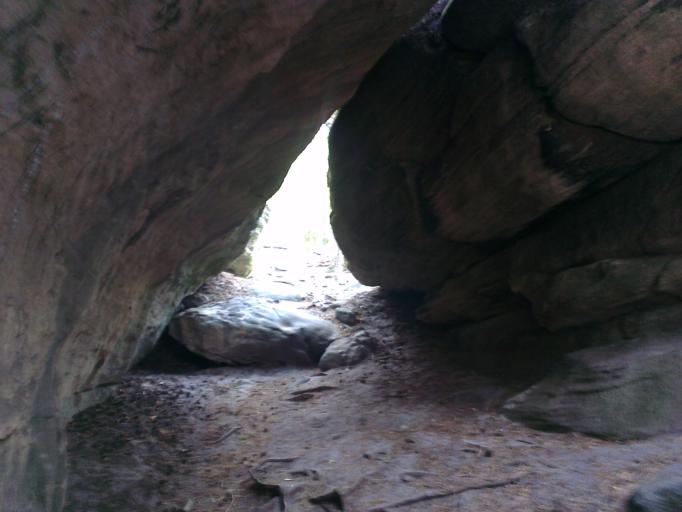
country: CZ
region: Pardubicky
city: Prosec
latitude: 49.8169
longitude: 16.1414
